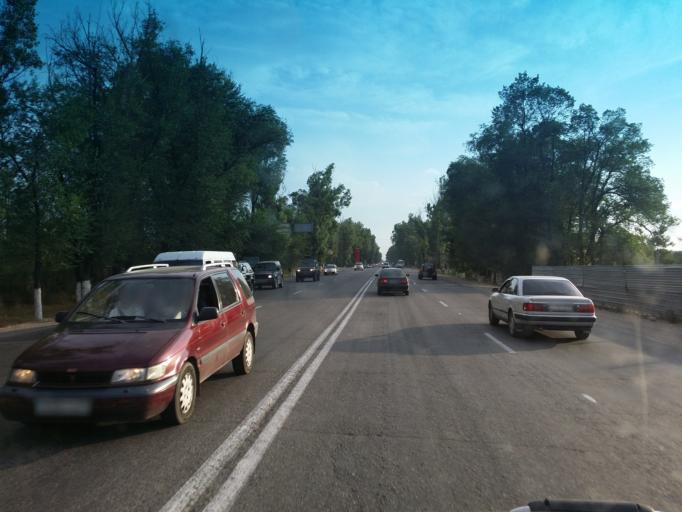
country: KZ
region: Almaty Oblysy
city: Energeticheskiy
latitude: 43.3654
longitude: 77.0851
